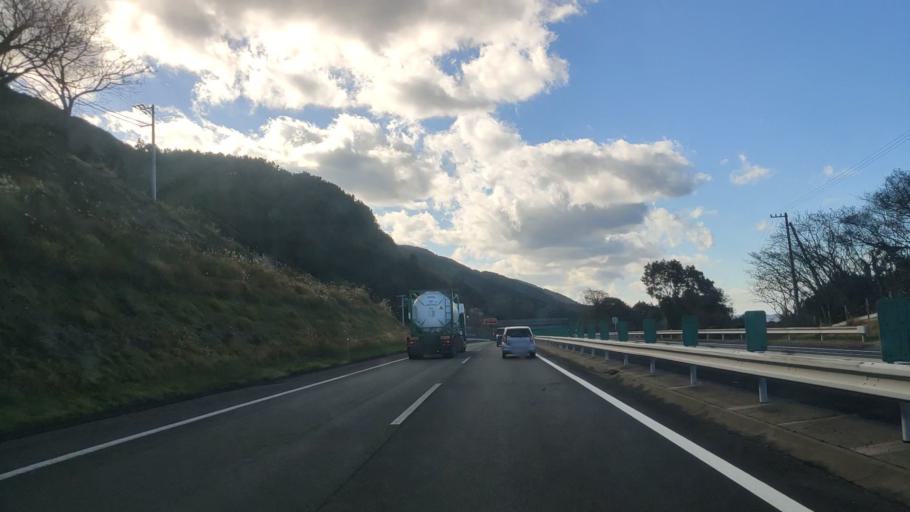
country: JP
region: Ehime
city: Kawanoecho
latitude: 33.9570
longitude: 133.4746
